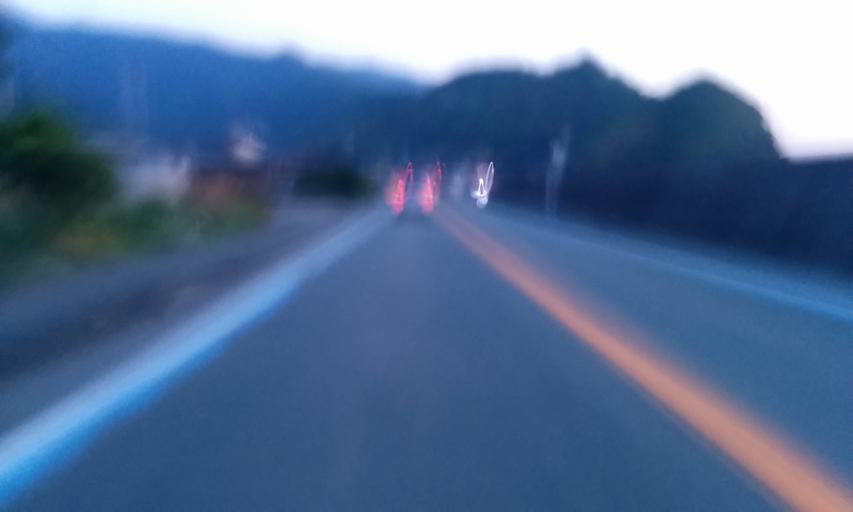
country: JP
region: Ehime
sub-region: Nishiuwa-gun
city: Ikata-cho
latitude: 33.5603
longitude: 132.4342
